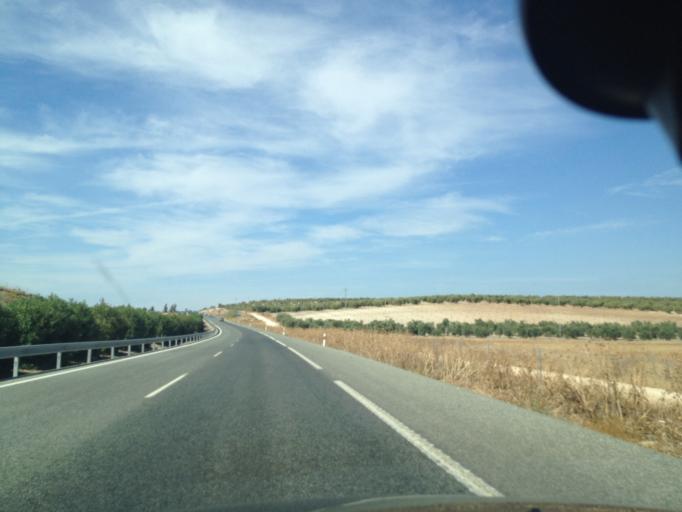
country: ES
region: Andalusia
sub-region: Provincia de Sevilla
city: La Puebla de Cazalla
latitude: 37.2314
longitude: -5.2445
